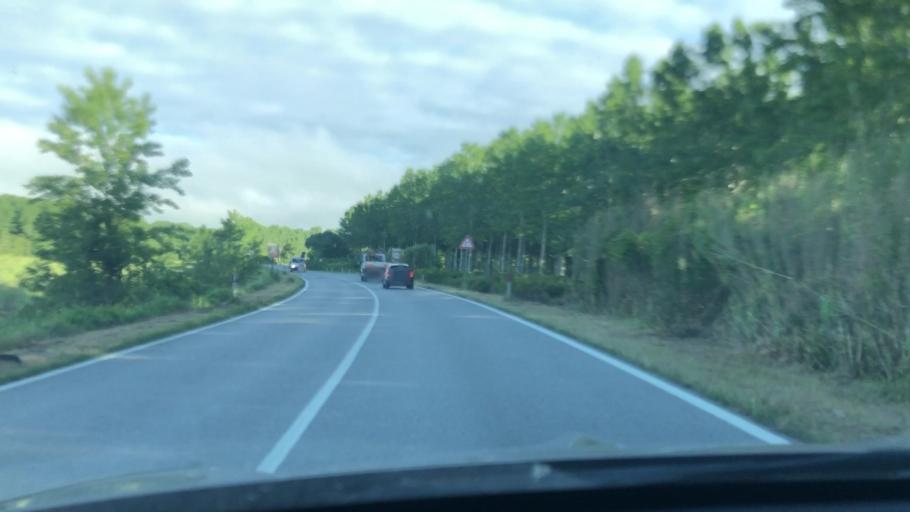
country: IT
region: Tuscany
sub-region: Province of Pisa
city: Forcoli
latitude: 43.6039
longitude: 10.6931
